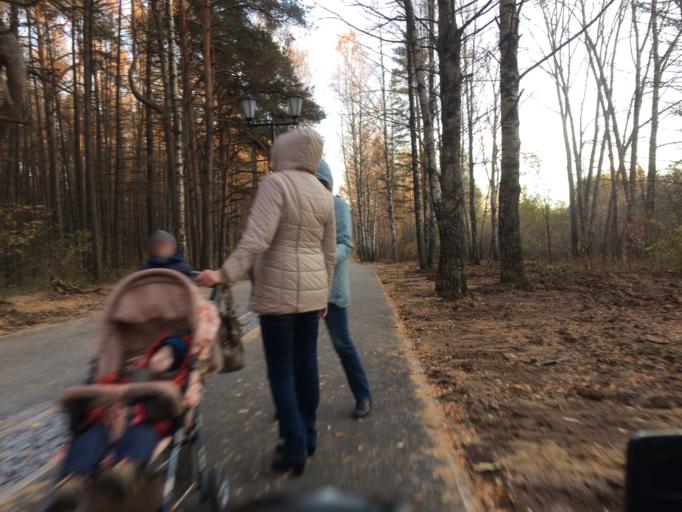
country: RU
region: Mariy-El
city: Yoshkar-Ola
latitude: 56.6248
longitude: 47.9168
